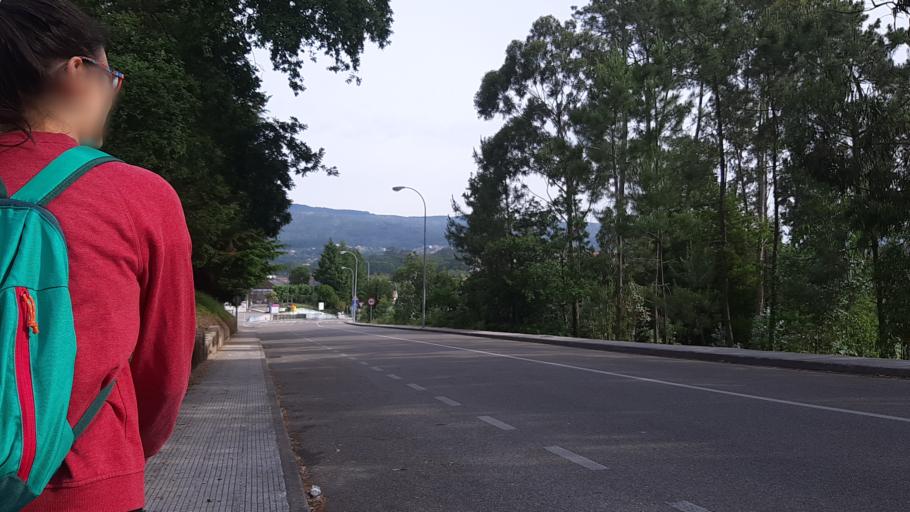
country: ES
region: Galicia
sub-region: Provincia de Pontevedra
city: O Rosal
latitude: 41.9286
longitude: -8.8364
